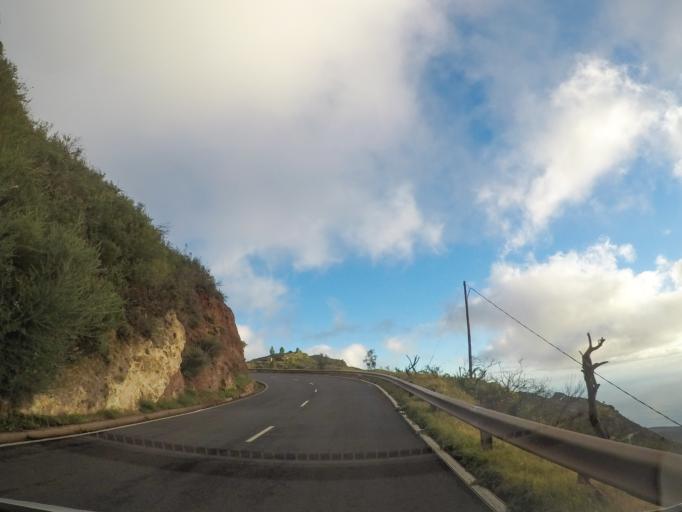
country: ES
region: Canary Islands
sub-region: Provincia de Santa Cruz de Tenerife
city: Alajero
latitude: 28.0883
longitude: -17.2513
